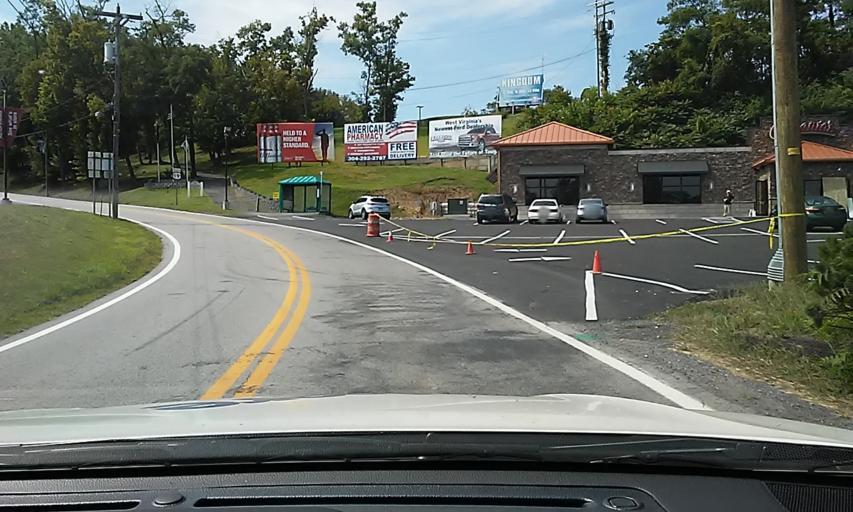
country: US
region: West Virginia
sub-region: Monongalia County
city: Westover
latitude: 39.6345
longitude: -79.9708
